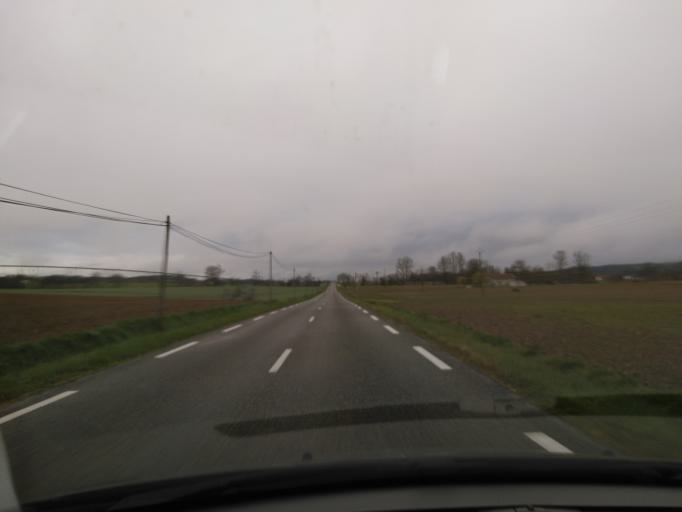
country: FR
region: Midi-Pyrenees
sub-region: Departement de la Haute-Garonne
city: Montesquieu-Volvestre
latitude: 43.1706
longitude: 1.2627
